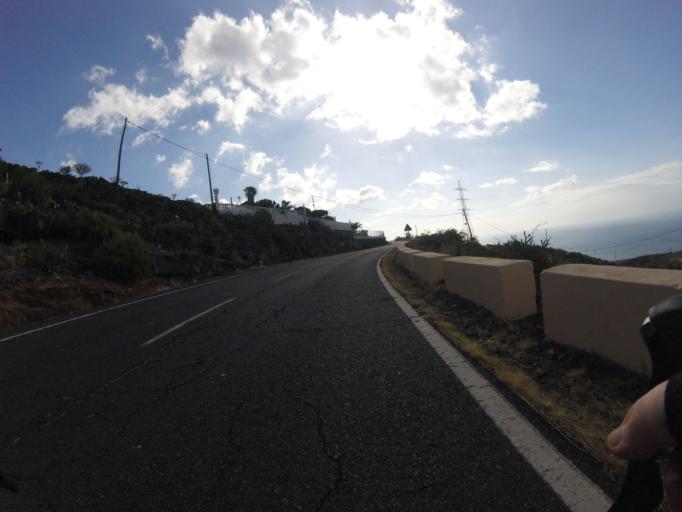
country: ES
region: Canary Islands
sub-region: Provincia de Santa Cruz de Tenerife
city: Candelaria
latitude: 28.4027
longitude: -16.3494
